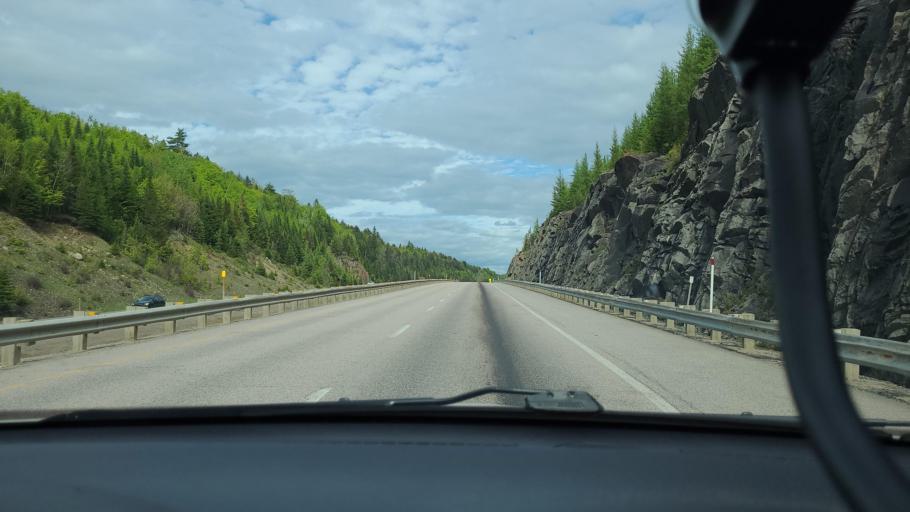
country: CA
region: Quebec
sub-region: Laurentides
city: Mont-Tremblant
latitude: 46.1569
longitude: -74.6788
